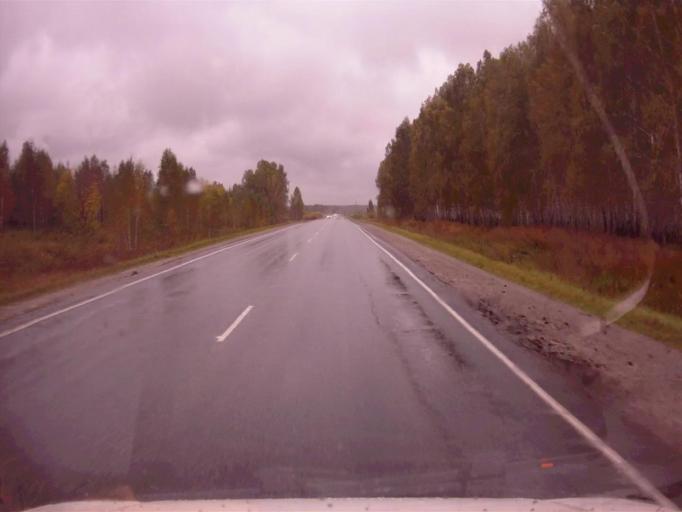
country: RU
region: Chelyabinsk
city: Argayash
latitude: 55.4789
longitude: 60.8223
